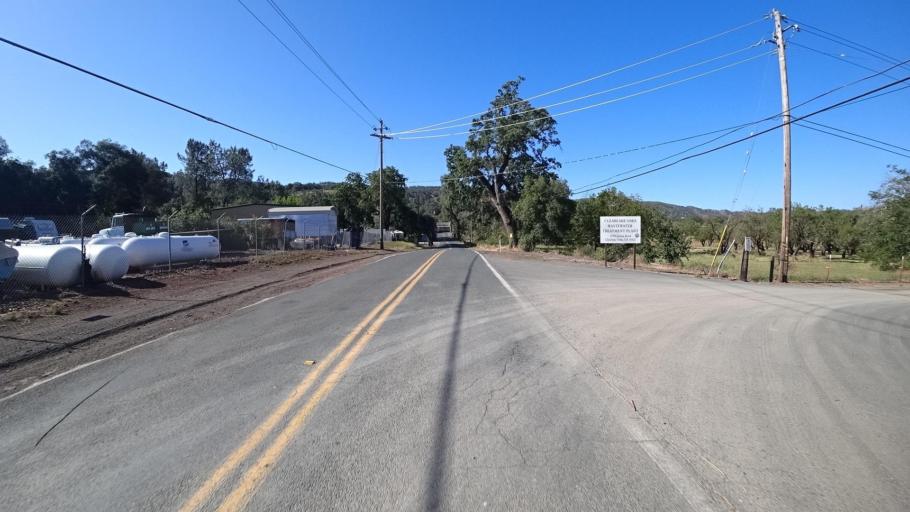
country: US
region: California
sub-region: Lake County
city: Clearlake Oaks
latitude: 39.0158
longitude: -122.6489
